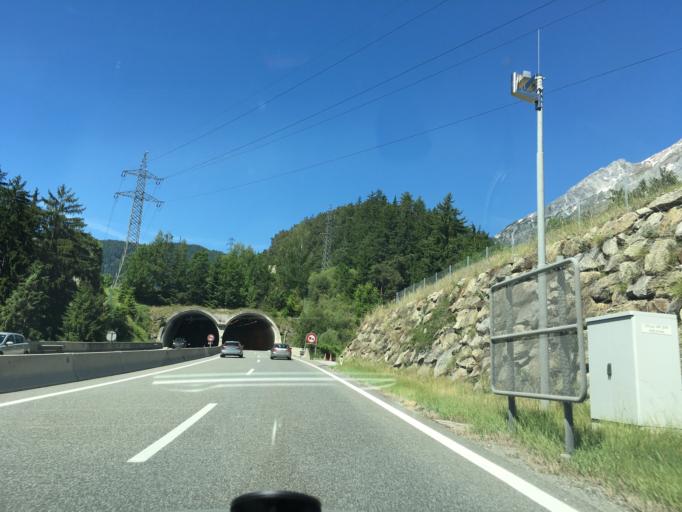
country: AT
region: Tyrol
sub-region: Politischer Bezirk Landeck
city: Grins
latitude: 47.1384
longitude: 10.5296
